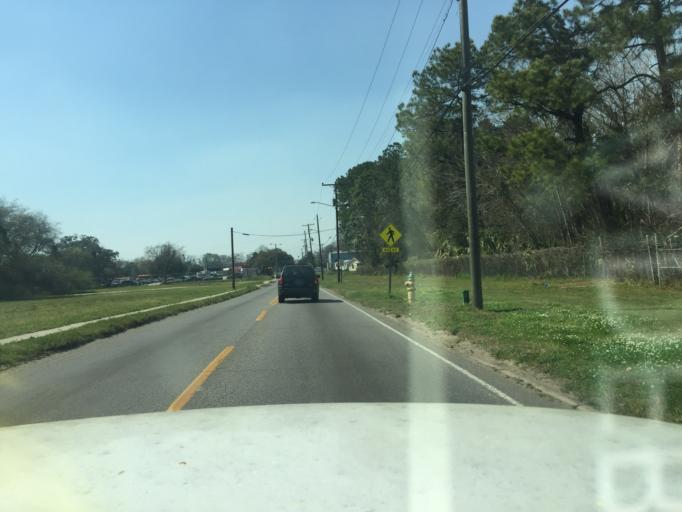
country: US
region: Georgia
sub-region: Chatham County
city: Savannah
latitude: 32.0709
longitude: -81.1108
